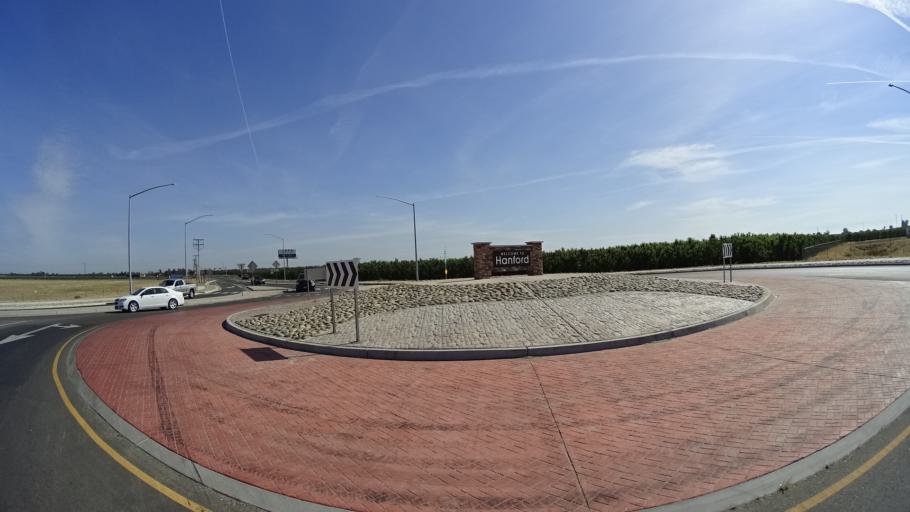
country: US
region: California
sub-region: Kings County
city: Home Garden
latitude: 36.3290
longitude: -119.6012
